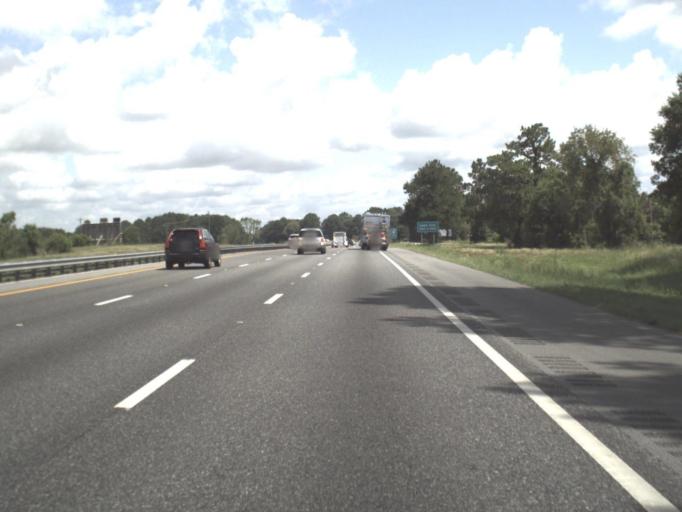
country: US
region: Florida
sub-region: Alachua County
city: High Springs
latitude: 29.9846
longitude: -82.5810
